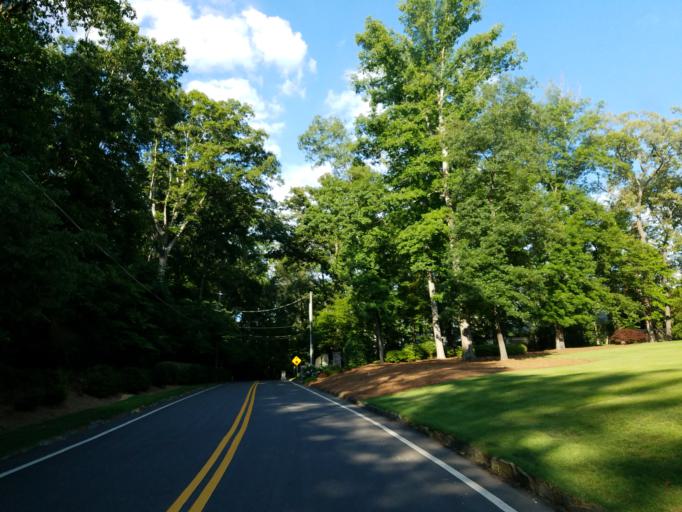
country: US
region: Georgia
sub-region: Cobb County
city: Vinings
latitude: 33.8798
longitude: -84.4267
